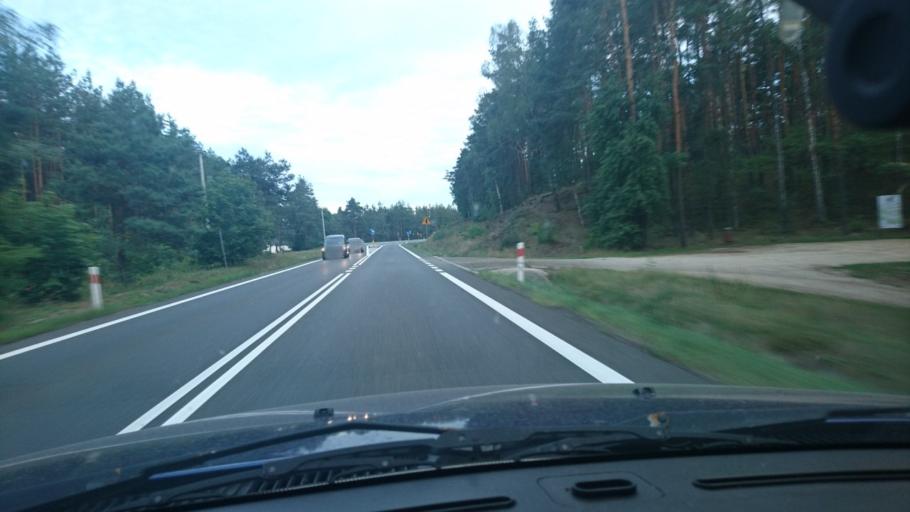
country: PL
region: Silesian Voivodeship
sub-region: Powiat tarnogorski
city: Tworog
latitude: 50.5994
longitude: 18.7021
